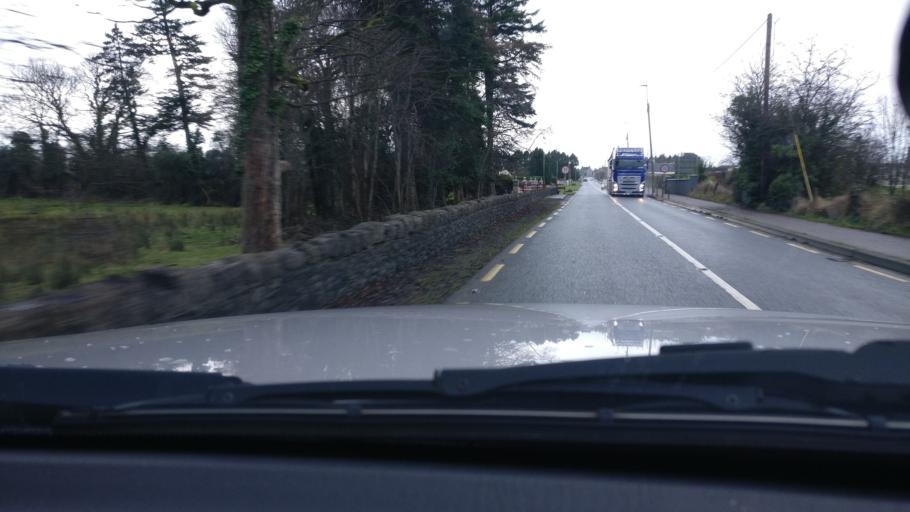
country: IE
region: Leinster
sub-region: An Longfort
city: Ballymahon
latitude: 53.5703
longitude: -7.7582
